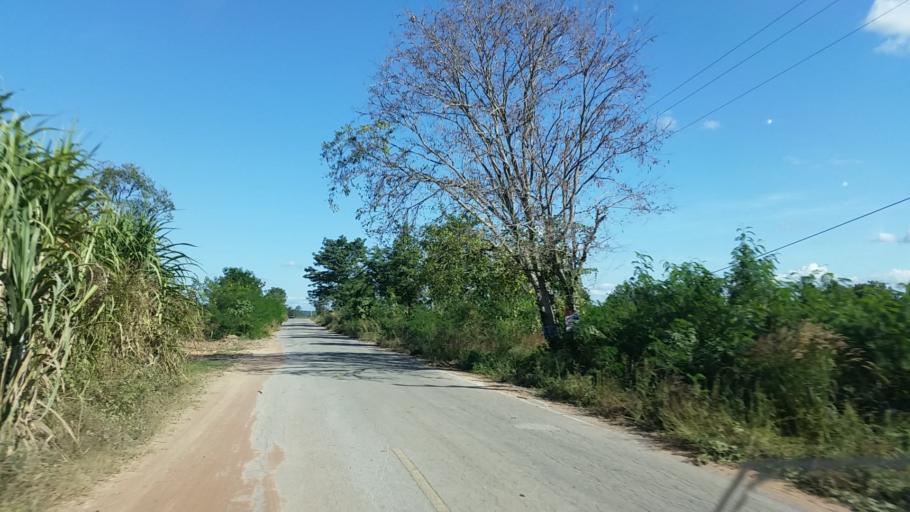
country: TH
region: Chaiyaphum
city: Thep Sathit
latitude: 15.5461
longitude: 101.4621
